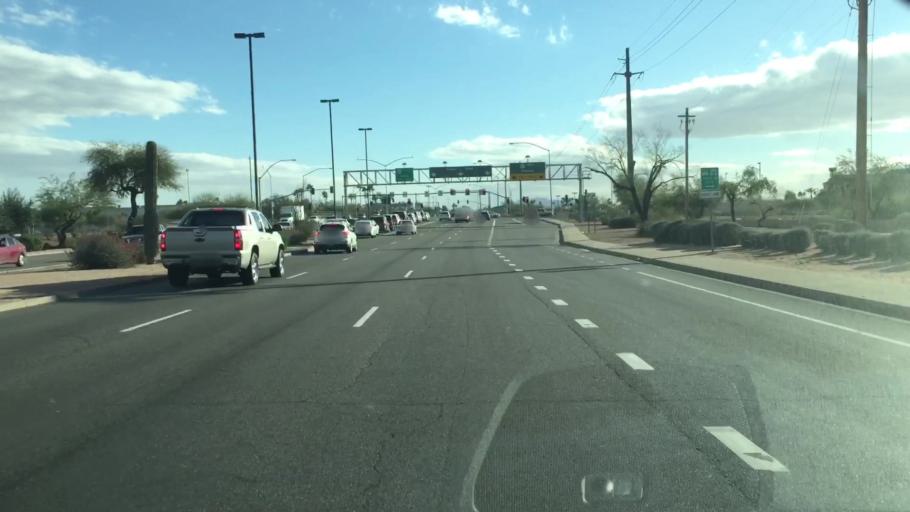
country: US
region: Arizona
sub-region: Maricopa County
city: Gilbert
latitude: 33.3888
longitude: -111.6849
